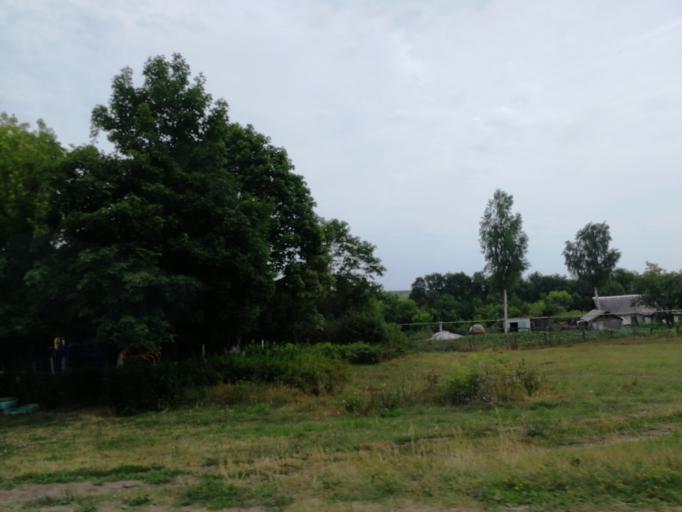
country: RU
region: Tula
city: Zhdankovskiy
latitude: 53.7039
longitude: 38.1566
